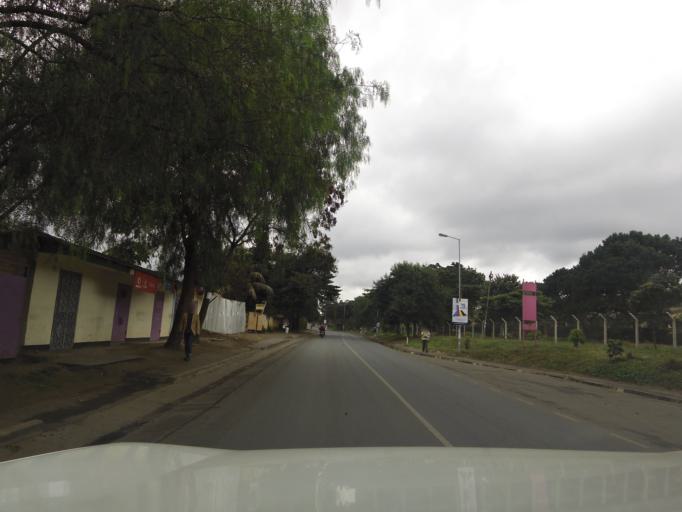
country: TZ
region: Arusha
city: Arusha
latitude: -3.3652
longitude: 36.6875
